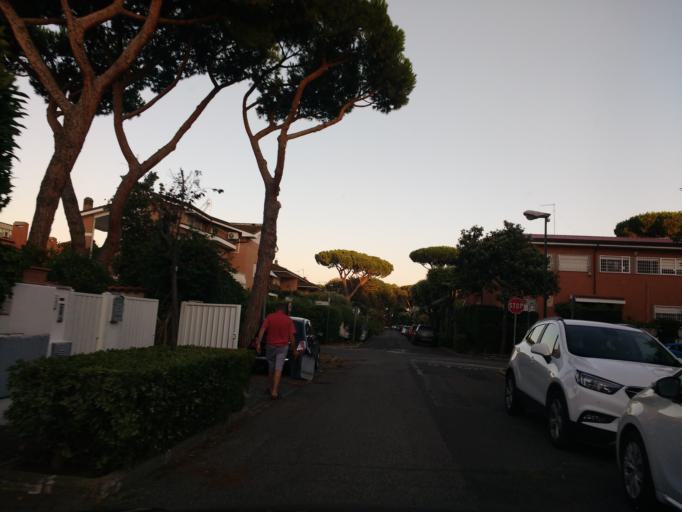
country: IT
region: Latium
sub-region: Citta metropolitana di Roma Capitale
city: Acilia-Castel Fusano-Ostia Antica
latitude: 41.7564
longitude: 12.3572
